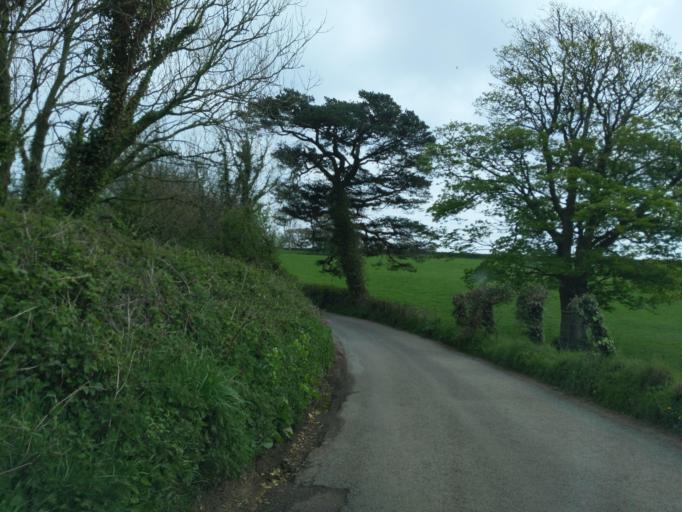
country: GB
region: England
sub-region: Devon
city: Dartmouth
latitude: 50.3577
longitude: -3.5467
